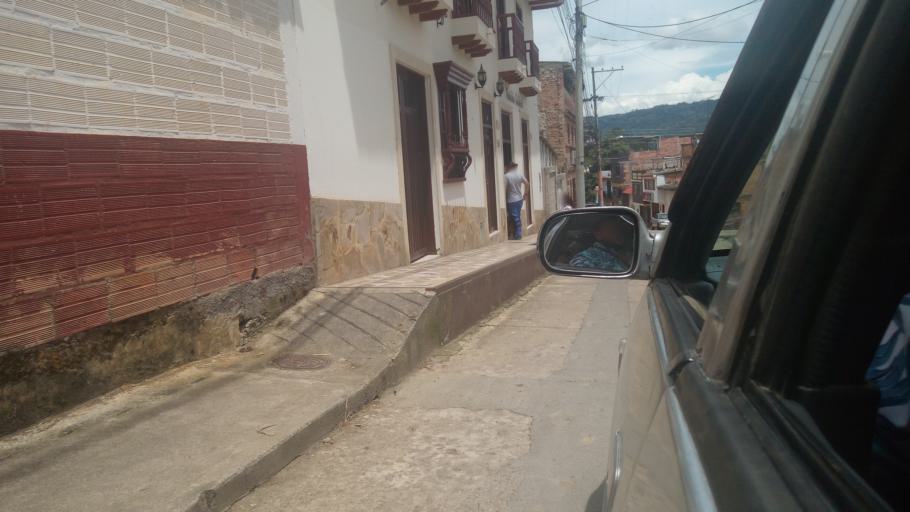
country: CO
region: Cundinamarca
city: Manta
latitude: 5.0092
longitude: -73.5410
